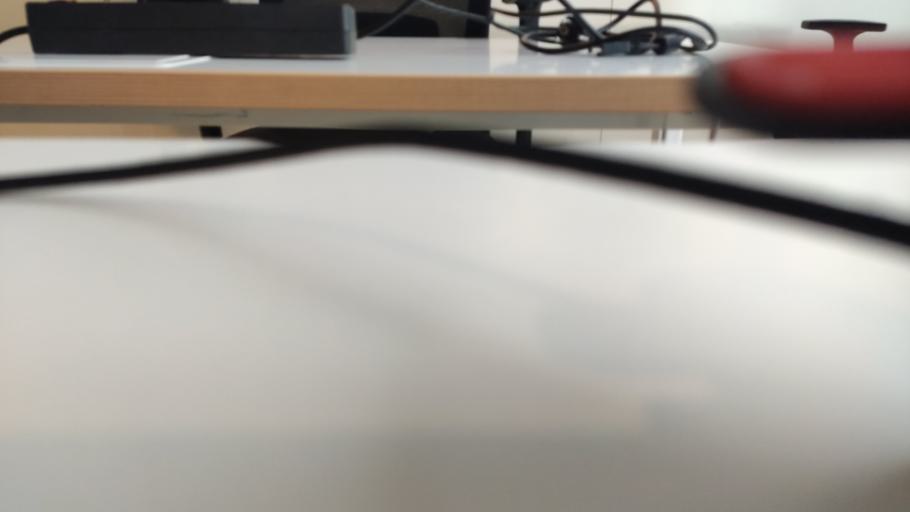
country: RU
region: Moskovskaya
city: Rogachevo
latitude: 56.4150
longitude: 37.0336
